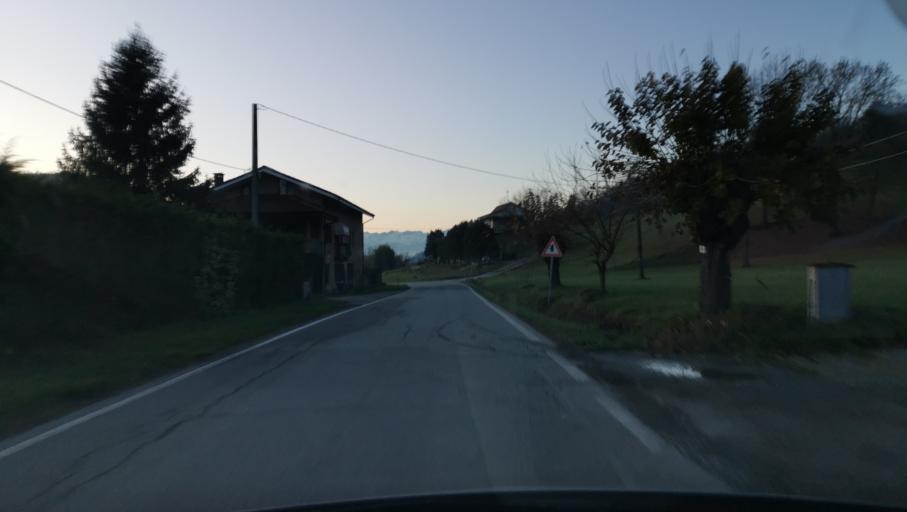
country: IT
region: Piedmont
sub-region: Provincia di Torino
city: Rivalba
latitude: 45.1192
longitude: 7.8646
